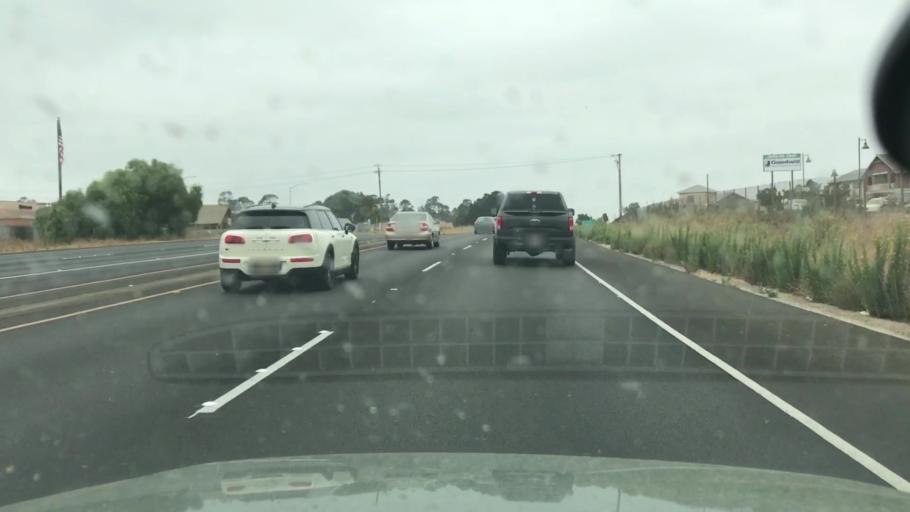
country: US
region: California
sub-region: Santa Barbara County
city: Orcutt
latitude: 34.8957
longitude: -120.4362
